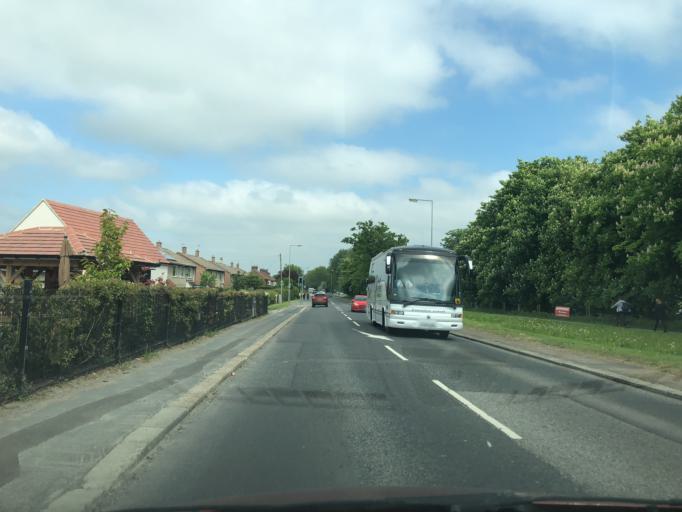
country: GB
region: England
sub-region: North Yorkshire
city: Catterick Garrison
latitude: 54.3777
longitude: -1.6927
